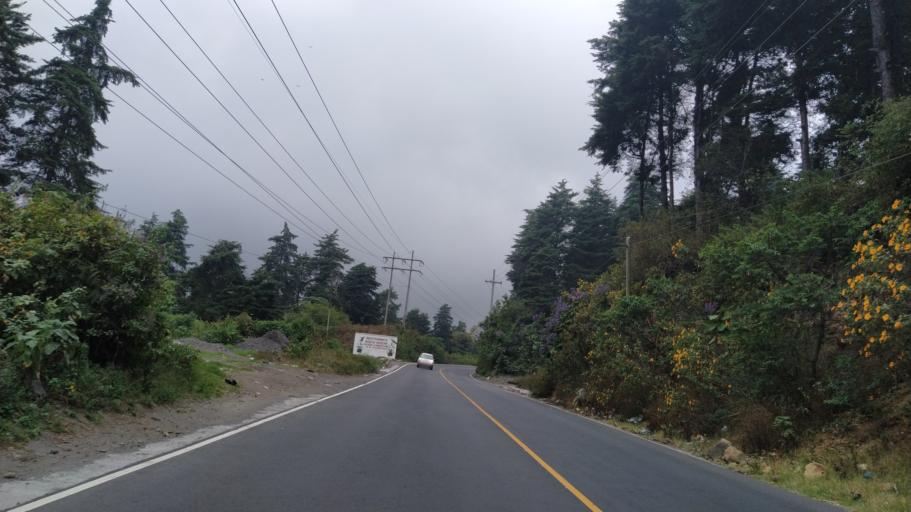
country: GT
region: Quetzaltenango
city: Zunil
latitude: 14.7407
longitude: -91.5168
